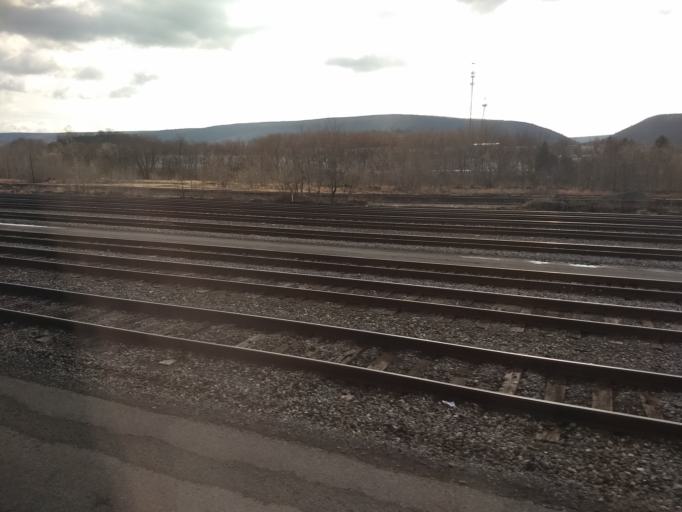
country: US
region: Pennsylvania
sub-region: Blair County
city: Altoona
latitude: 40.5263
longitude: -78.3883
